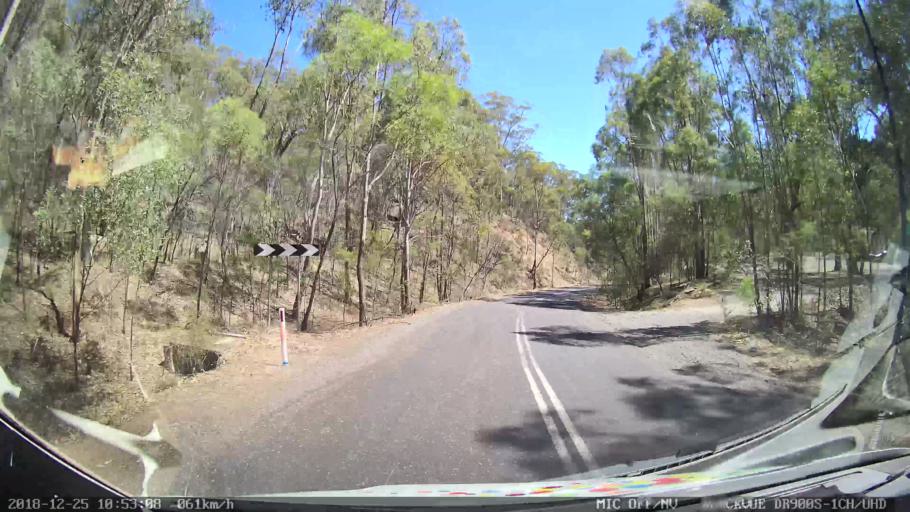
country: AU
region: New South Wales
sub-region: Upper Hunter Shire
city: Merriwa
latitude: -32.4226
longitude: 150.2729
